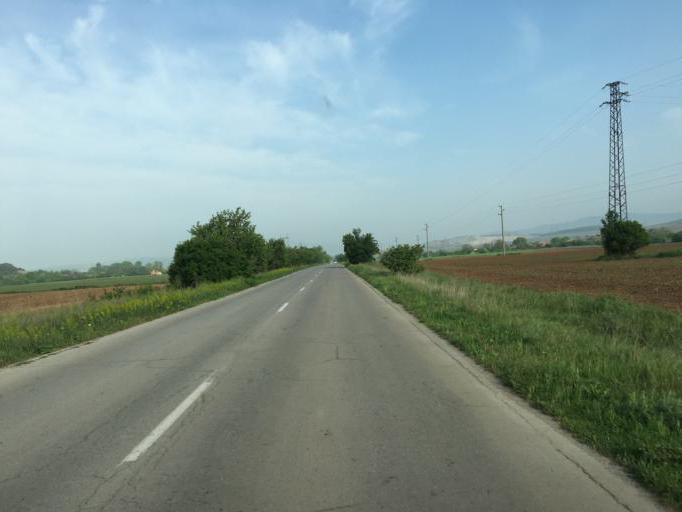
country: BG
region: Pernik
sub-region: Obshtina Radomir
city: Radomir
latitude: 42.4826
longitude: 23.0563
